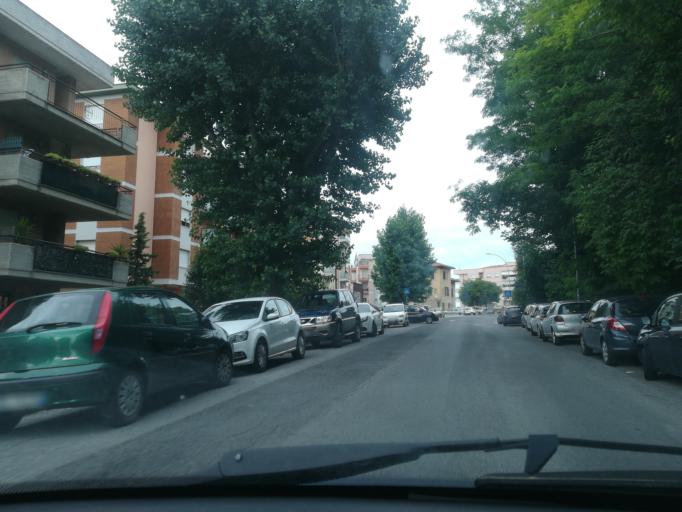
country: IT
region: The Marches
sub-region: Provincia di Macerata
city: Macerata
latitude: 43.3023
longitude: 13.4380
